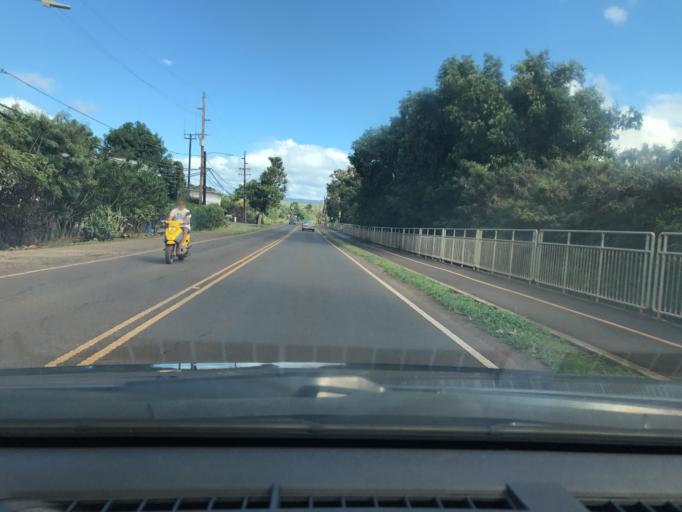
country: US
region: Hawaii
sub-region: Honolulu County
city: Waialua
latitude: 21.5757
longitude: -158.1183
